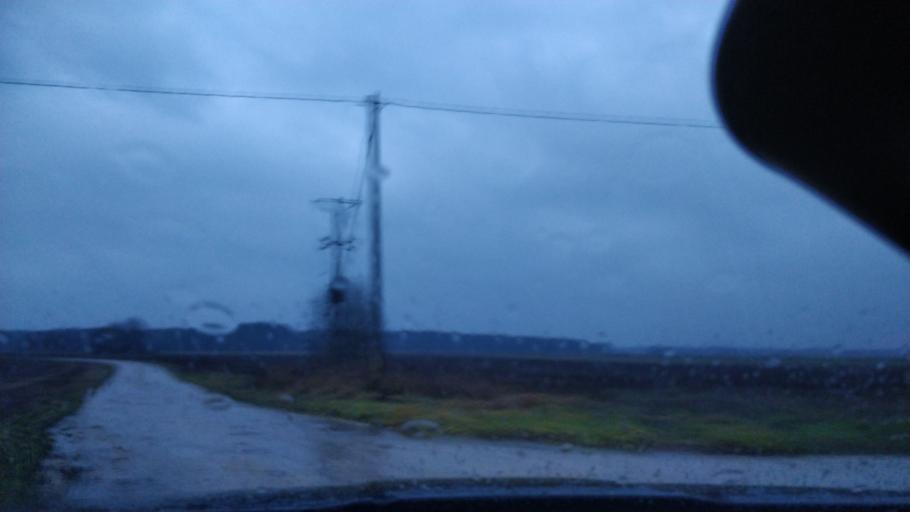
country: EE
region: Laeaene
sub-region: Lihula vald
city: Lihula
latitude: 58.8487
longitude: 23.9855
